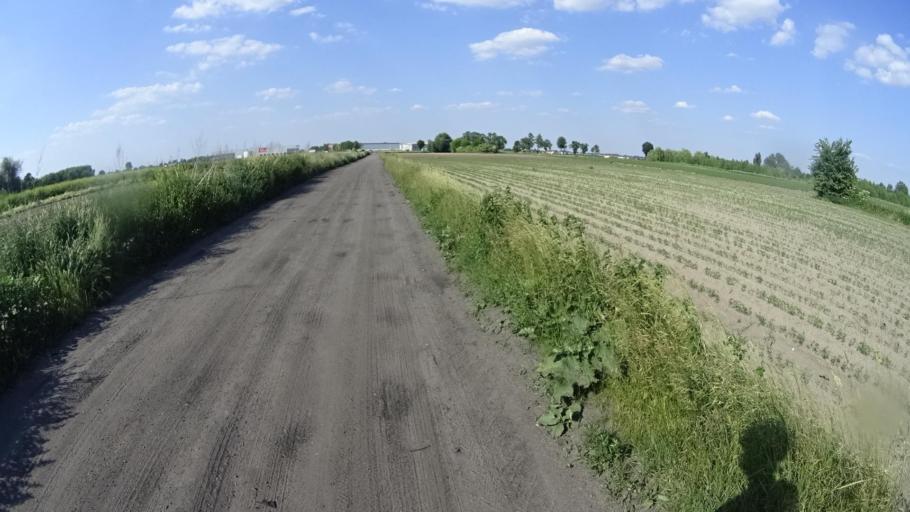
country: PL
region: Masovian Voivodeship
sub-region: Powiat warszawski zachodni
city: Ozarow Mazowiecki
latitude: 52.1962
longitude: 20.7650
